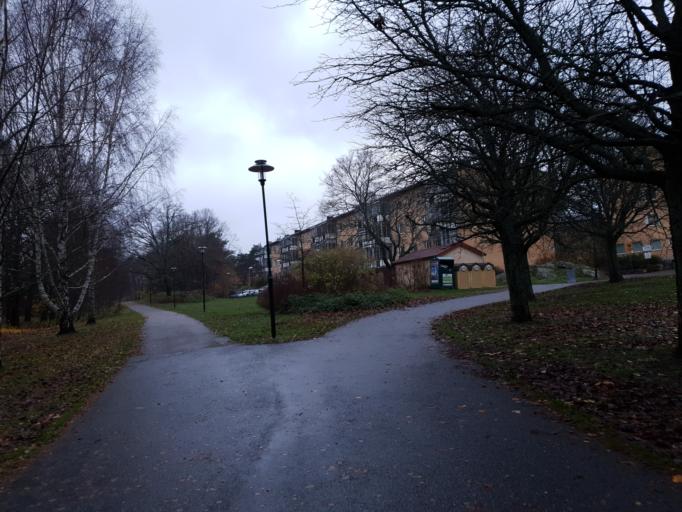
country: SE
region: Stockholm
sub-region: Stockholms Kommun
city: Arsta
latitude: 59.2412
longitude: 18.0850
